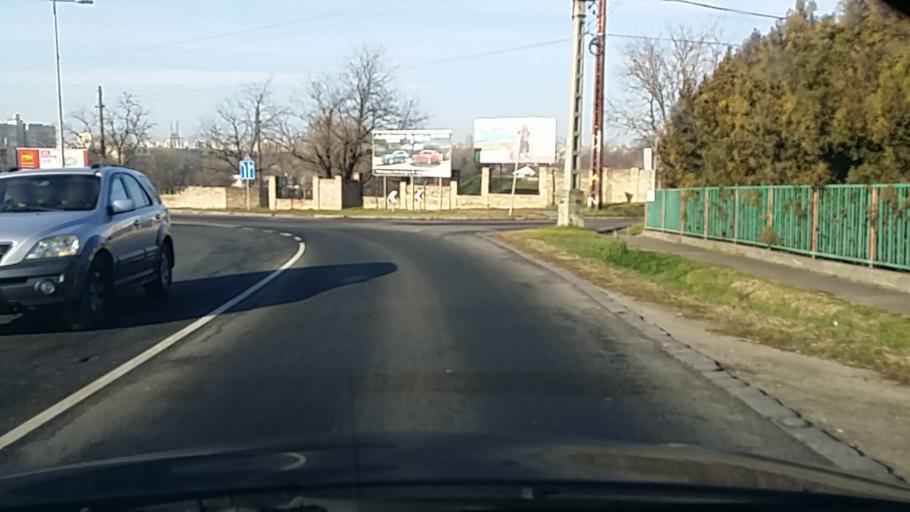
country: HU
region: Budapest
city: Budapest XVIII. keruelet
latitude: 47.4334
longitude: 19.1789
